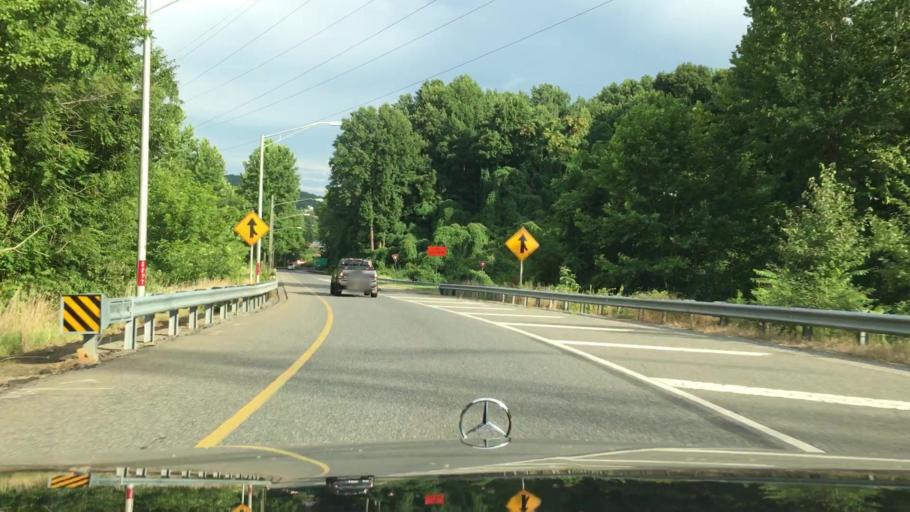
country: US
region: Virginia
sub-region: City of Lynchburg
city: West Lynchburg
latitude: 37.3627
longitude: -79.1844
